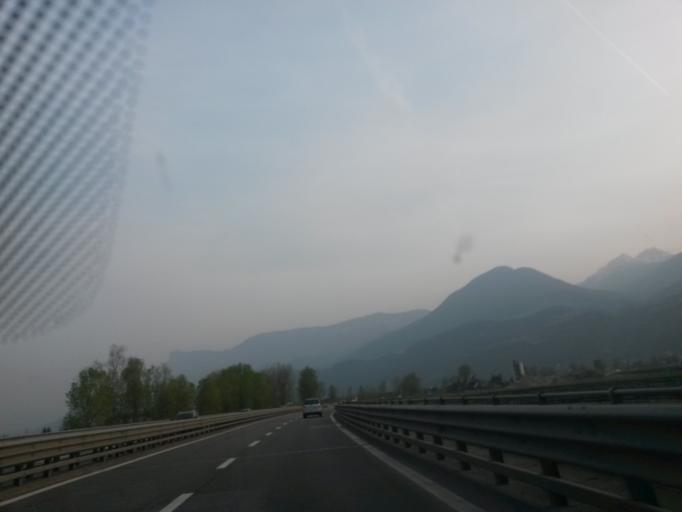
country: IT
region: Trentino-Alto Adige
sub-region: Bolzano
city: Postal
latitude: 46.6178
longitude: 11.1838
